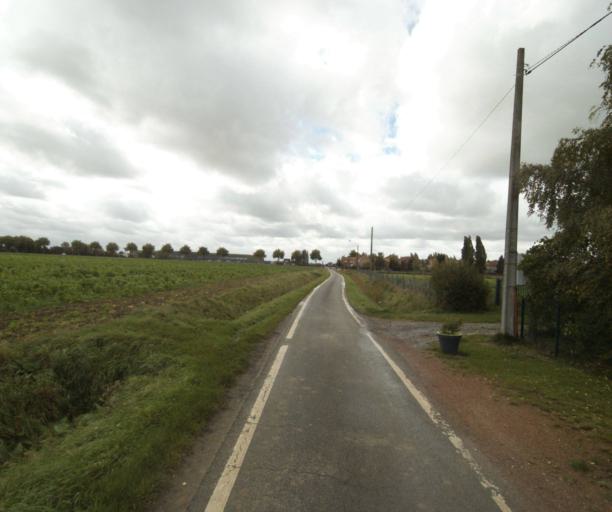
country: FR
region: Nord-Pas-de-Calais
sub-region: Departement du Nord
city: Houplines
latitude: 50.6666
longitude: 2.9233
